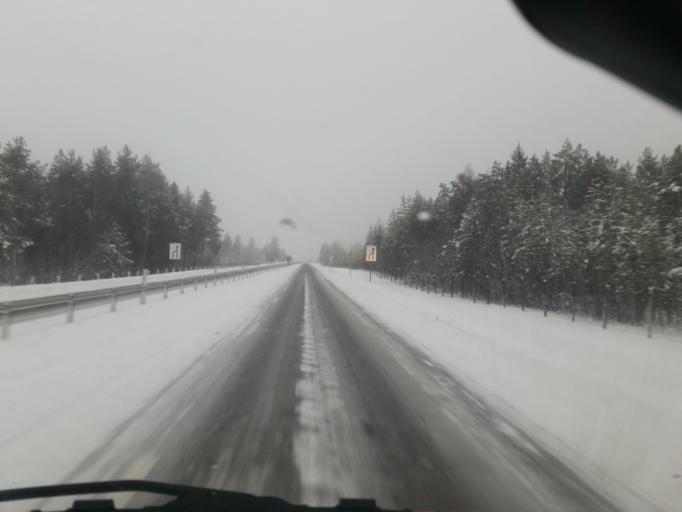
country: SE
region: Norrbotten
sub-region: Pitea Kommun
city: Pitea
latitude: 65.1802
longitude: 21.5042
